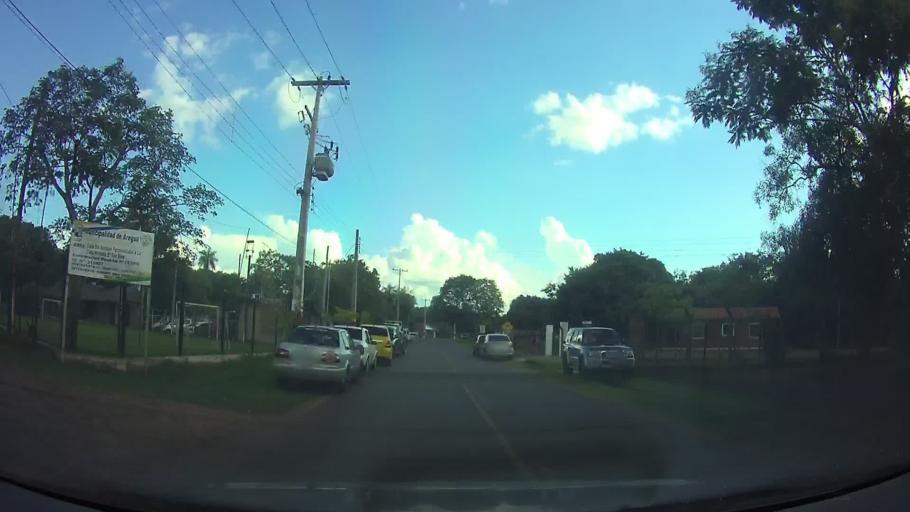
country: PY
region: Central
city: Aregua
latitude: -25.2733
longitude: -57.4301
